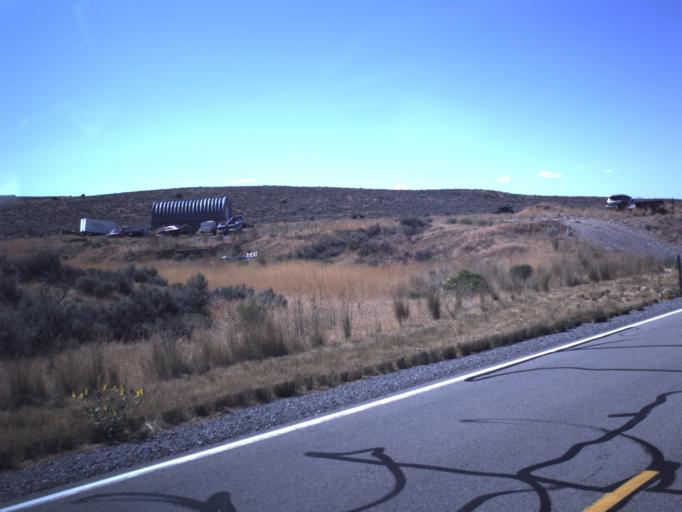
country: US
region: Utah
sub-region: Tooele County
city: Tooele
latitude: 40.4378
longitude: -112.3726
